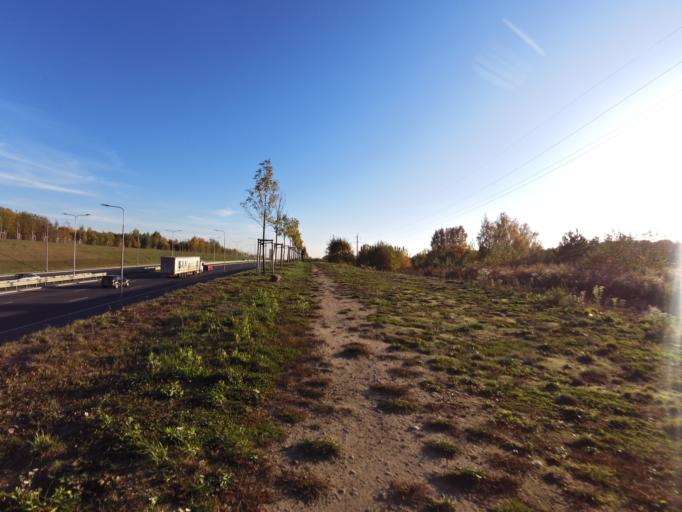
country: LT
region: Vilnius County
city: Justiniskes
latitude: 54.7190
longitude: 25.2078
